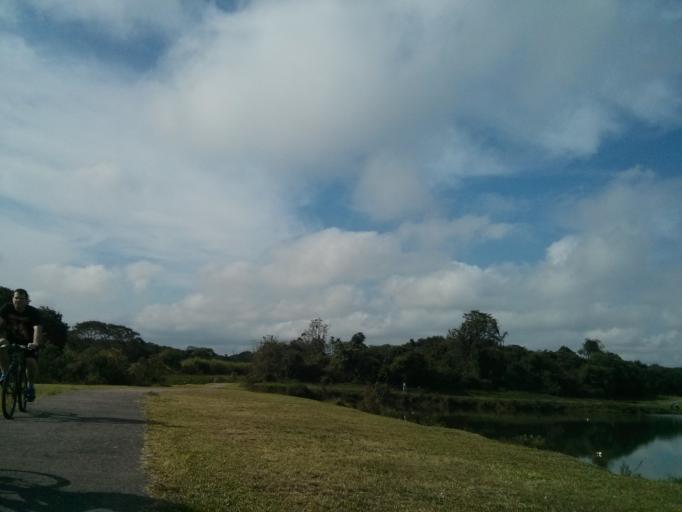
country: BR
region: Parana
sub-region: Sao Jose Dos Pinhais
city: Sao Jose dos Pinhais
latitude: -25.5091
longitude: -49.2149
